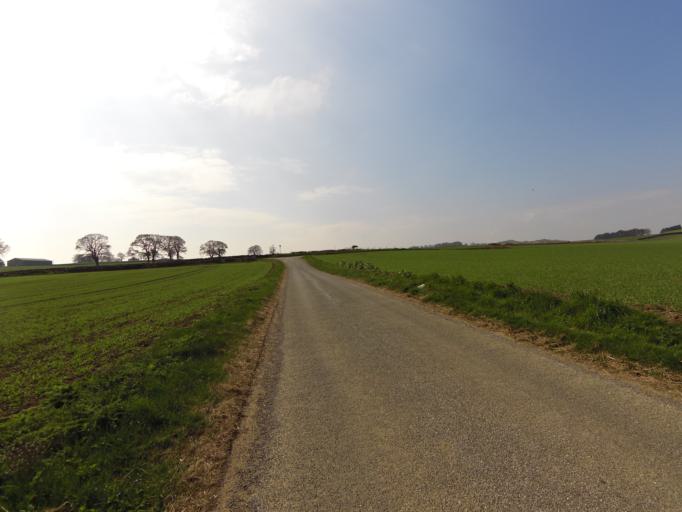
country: GB
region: Scotland
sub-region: Fife
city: Kinghorn
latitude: 56.0863
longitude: -3.1854
